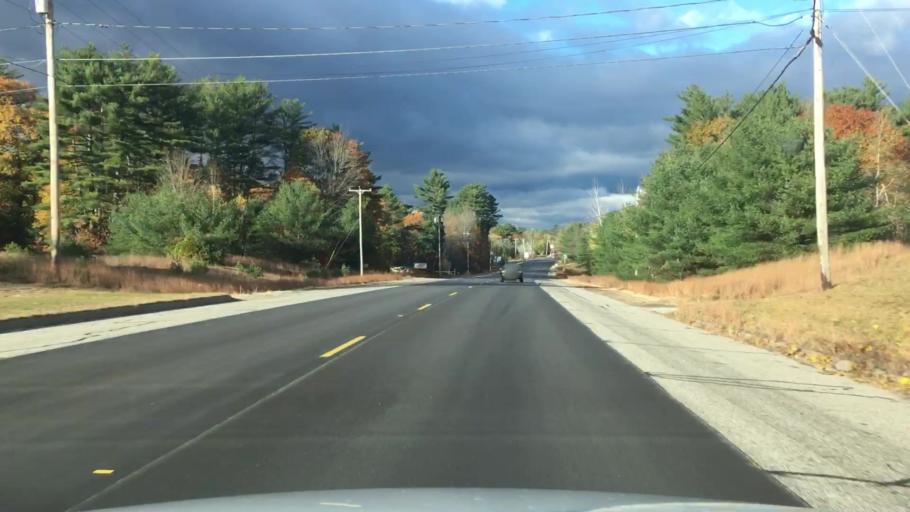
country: US
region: Maine
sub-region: Androscoggin County
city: Livermore
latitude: 44.3587
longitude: -70.2554
